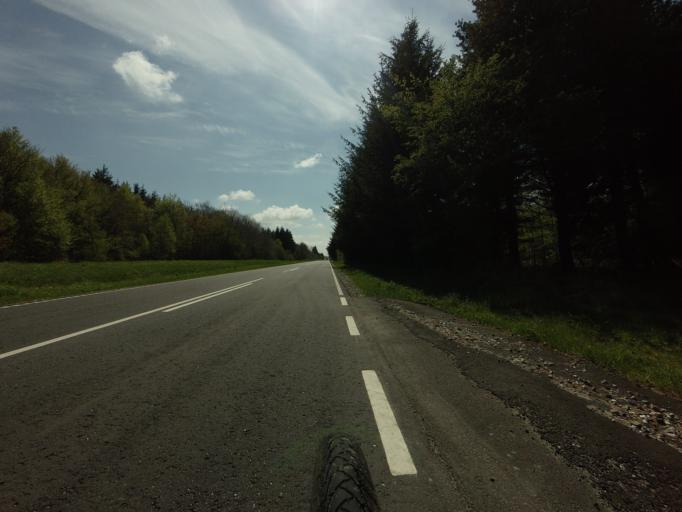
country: DK
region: North Denmark
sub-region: Jammerbugt Kommune
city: Brovst
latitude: 57.1611
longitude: 9.5755
